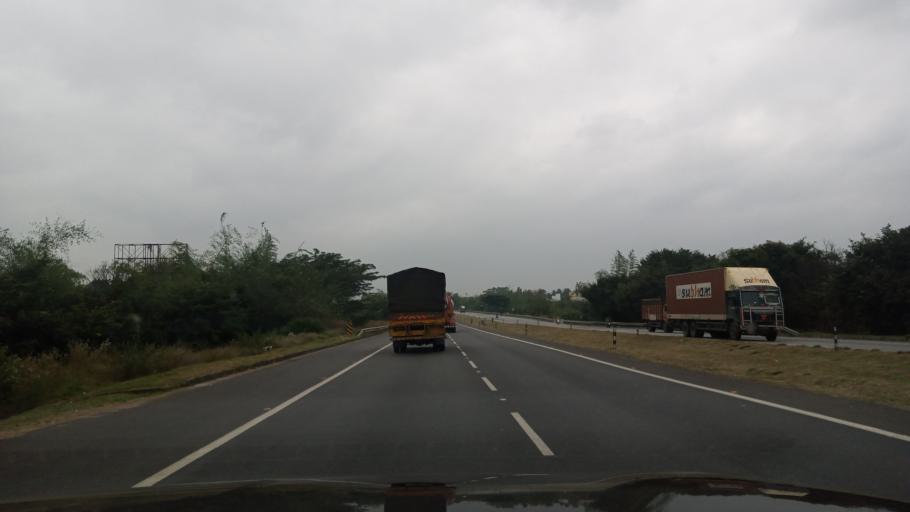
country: IN
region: Karnataka
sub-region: Bangalore Rural
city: Nelamangala
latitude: 13.0330
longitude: 77.4758
